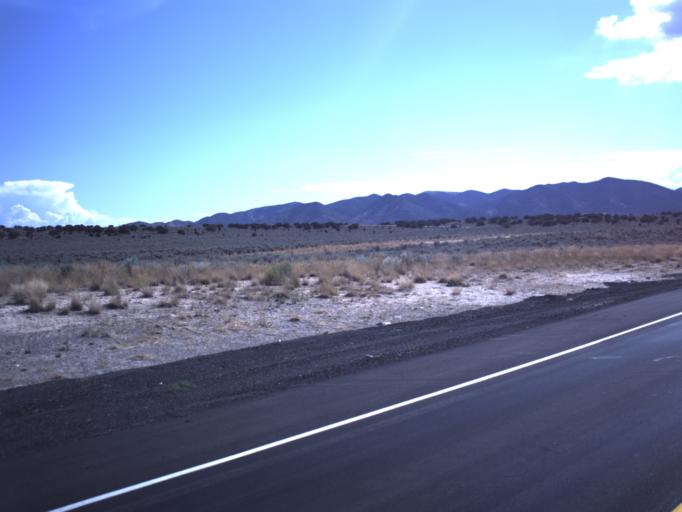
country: US
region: Utah
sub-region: Utah County
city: Eagle Mountain
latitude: 40.0553
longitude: -112.3024
